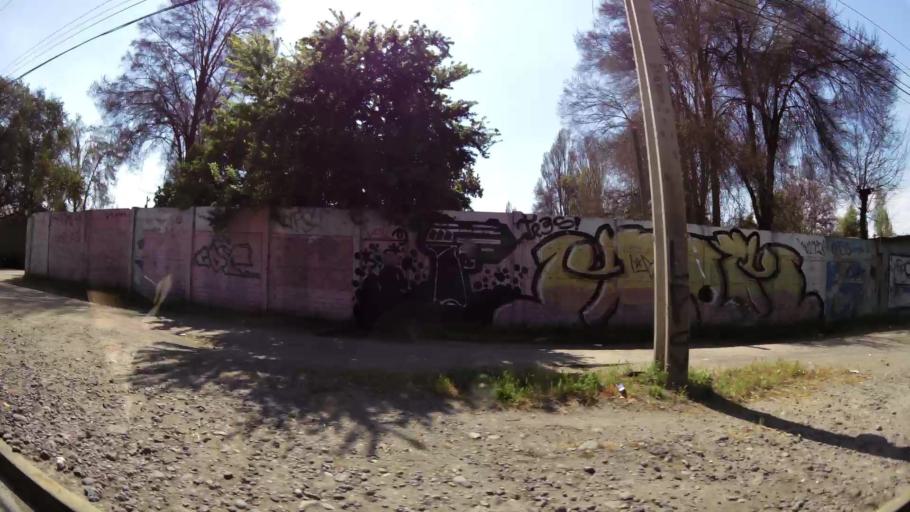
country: CL
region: Santiago Metropolitan
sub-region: Provincia de Cordillera
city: Puente Alto
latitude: -33.6159
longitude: -70.6056
